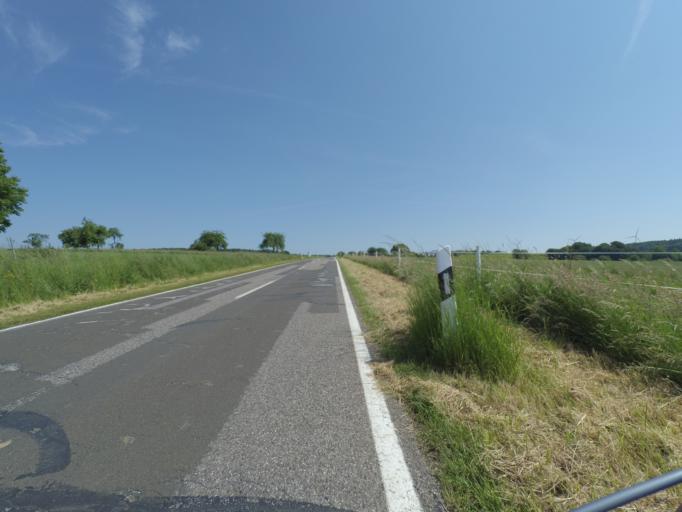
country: DE
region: Rheinland-Pfalz
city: Spesenroth
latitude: 50.0440
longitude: 7.4502
